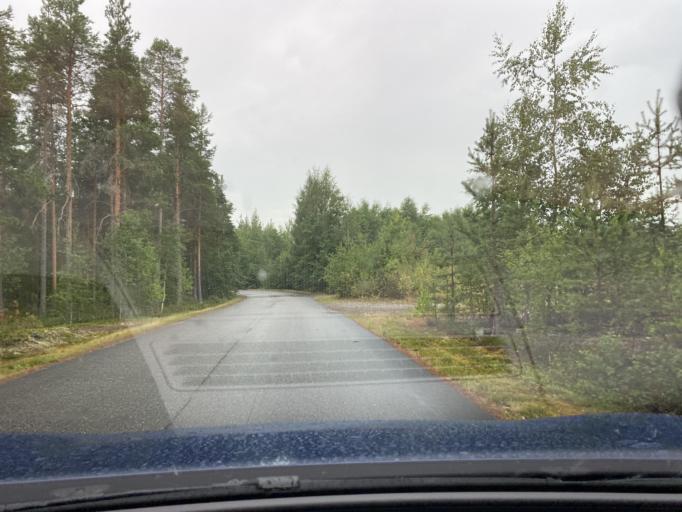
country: FI
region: Central Ostrobothnia
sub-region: Kaustinen
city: Halsua
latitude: 63.4130
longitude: 23.9739
